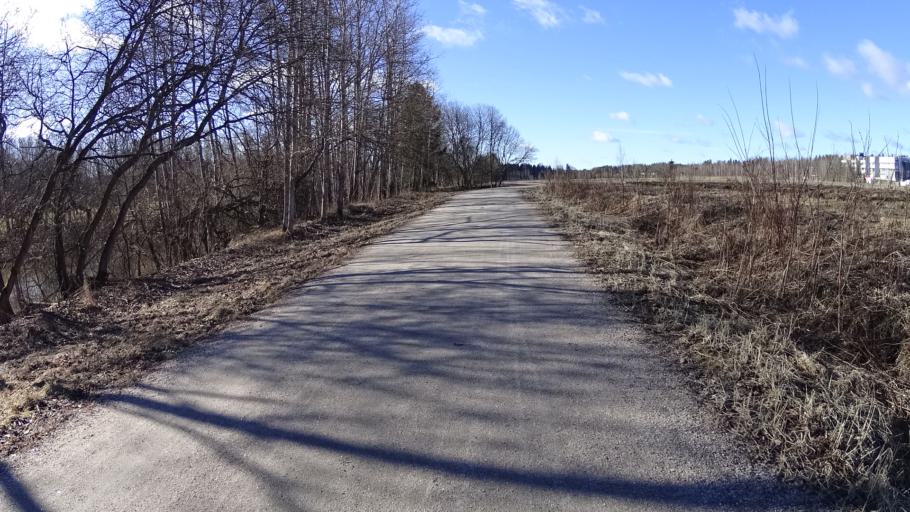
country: FI
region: Uusimaa
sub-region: Helsinki
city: Teekkarikylae
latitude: 60.2844
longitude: 24.8856
